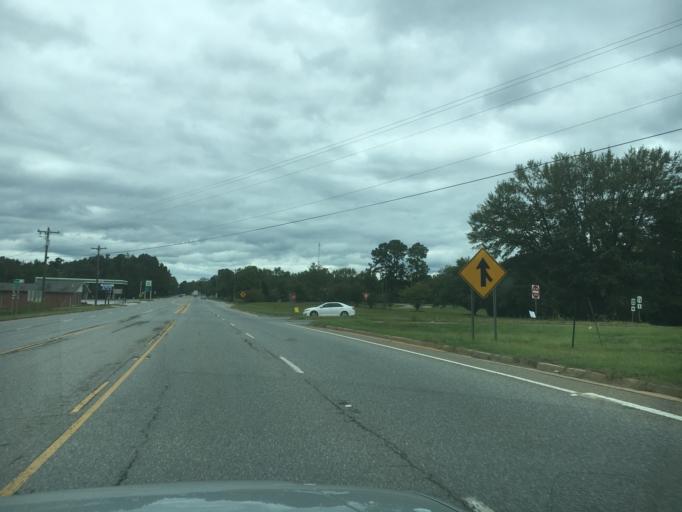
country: US
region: South Carolina
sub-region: Greenwood County
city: Ware Shoals
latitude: 34.5003
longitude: -82.2893
